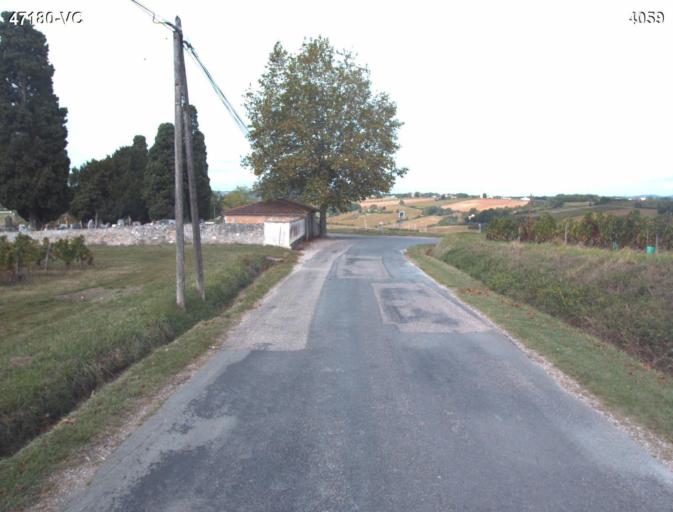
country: FR
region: Aquitaine
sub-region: Departement du Lot-et-Garonne
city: Sainte-Colombe-en-Bruilhois
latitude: 44.1622
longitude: 0.4567
